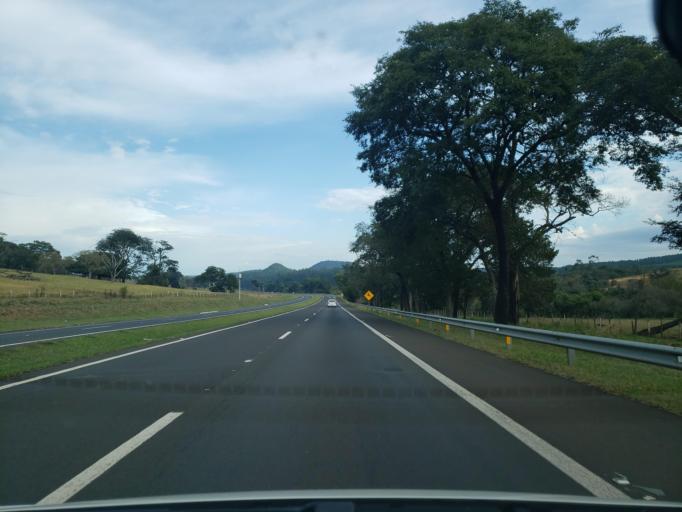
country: BR
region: Sao Paulo
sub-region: Itirapina
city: Itirapina
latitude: -22.2740
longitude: -47.9517
